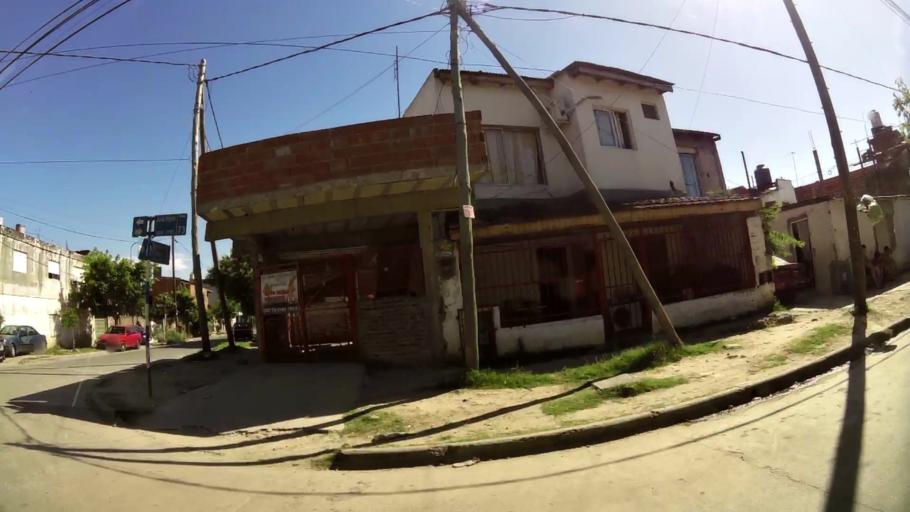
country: AR
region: Buenos Aires
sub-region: Partido de General San Martin
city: General San Martin
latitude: -34.5339
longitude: -58.5807
